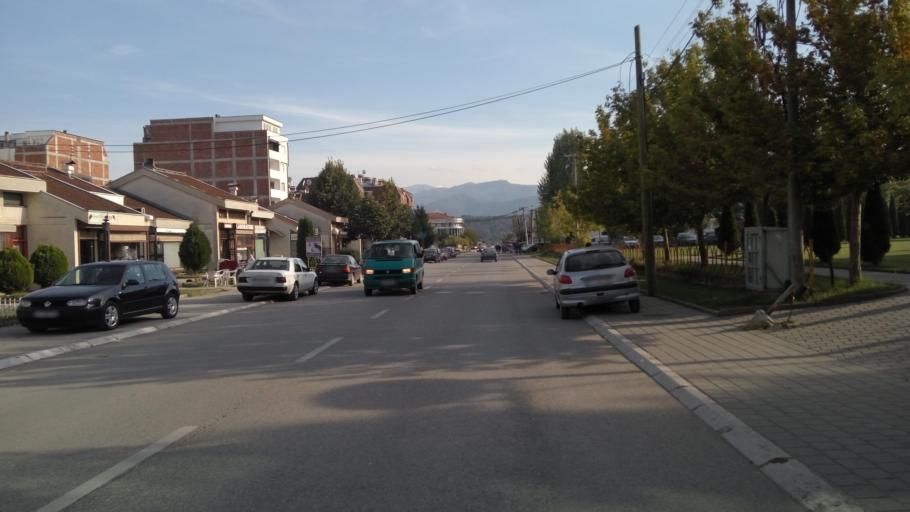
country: XK
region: Gjakova
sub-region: Komuna e Gjakoves
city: Gjakove
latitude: 42.3742
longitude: 20.4336
